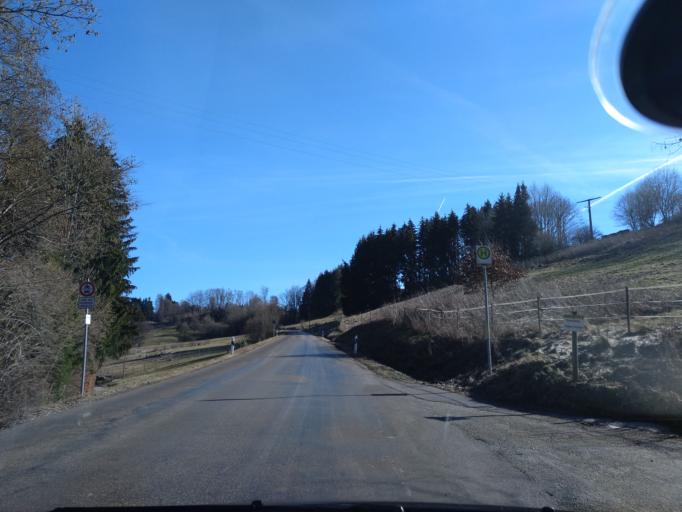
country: DE
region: Baden-Wuerttemberg
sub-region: Regierungsbezirk Stuttgart
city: Mainhardt
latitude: 49.0856
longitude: 9.5565
